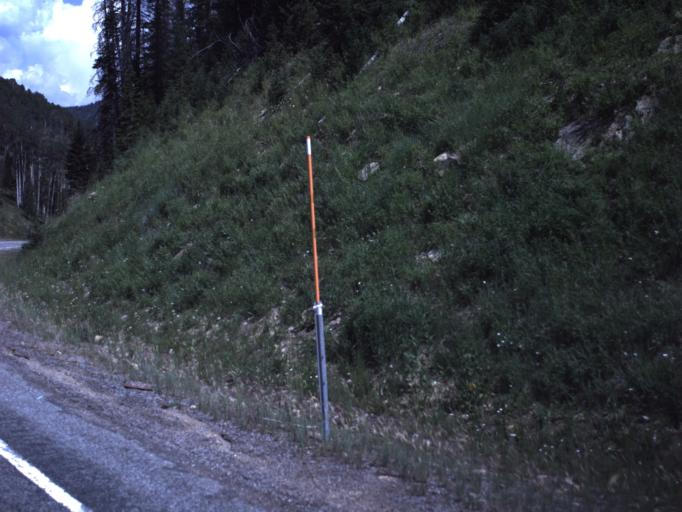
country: US
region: Utah
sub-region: Sanpete County
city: Fairview
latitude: 39.5945
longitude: -111.2281
